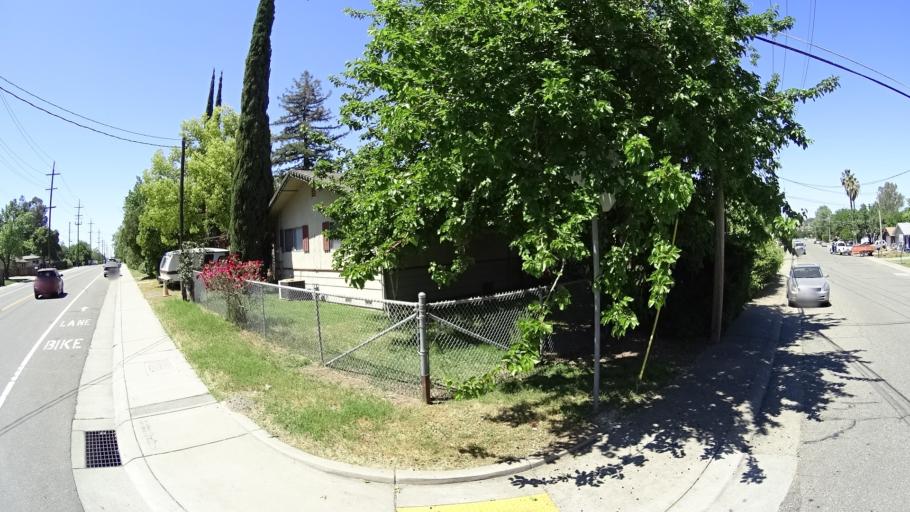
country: US
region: California
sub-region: Placer County
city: Rocklin
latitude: 38.7938
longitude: -121.2292
